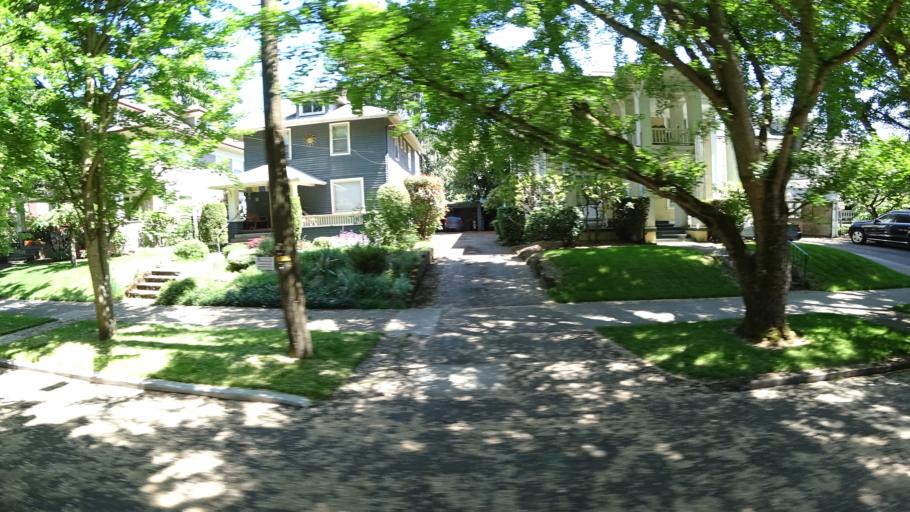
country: US
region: Oregon
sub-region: Multnomah County
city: Portland
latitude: 45.5410
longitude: -122.6495
